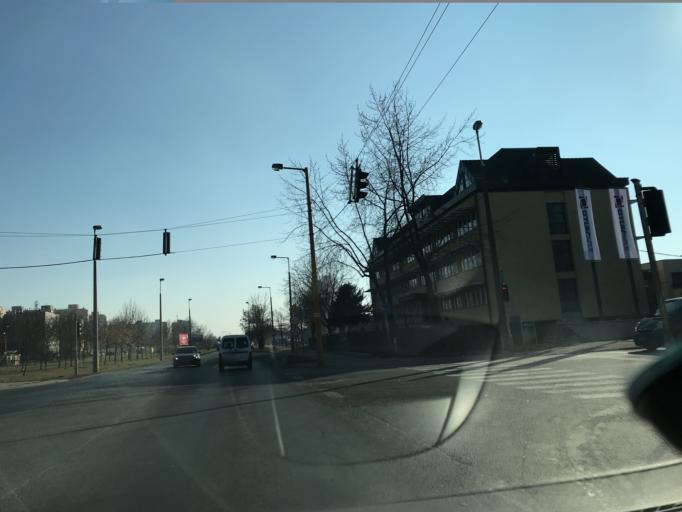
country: HU
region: Gyor-Moson-Sopron
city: Gyor
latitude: 47.6709
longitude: 17.6343
